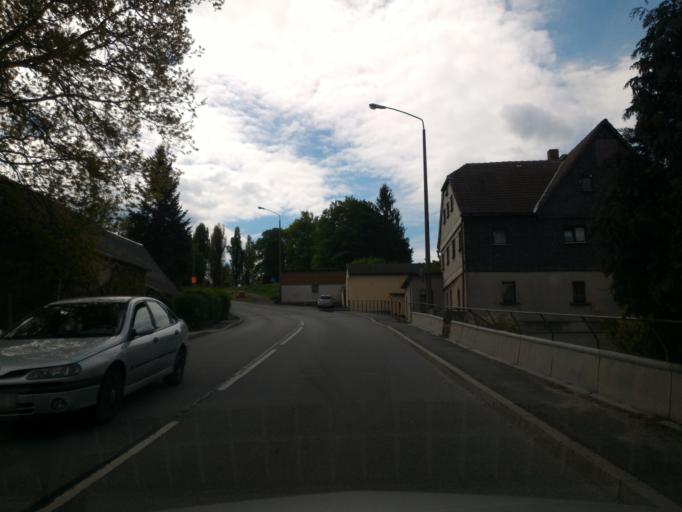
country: DE
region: Saxony
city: Neugersdorf
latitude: 50.9712
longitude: 14.5975
